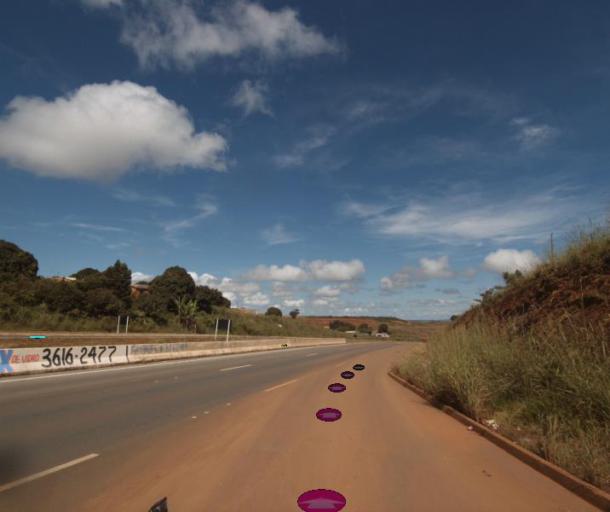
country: BR
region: Federal District
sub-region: Brasilia
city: Brasilia
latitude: -15.7548
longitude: -48.3296
